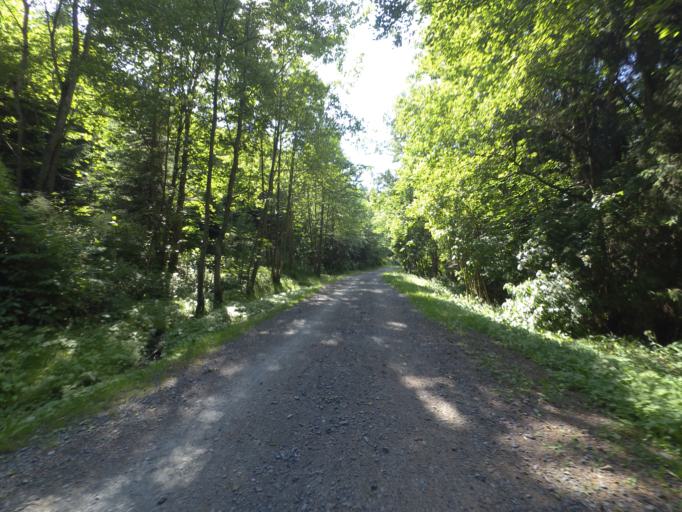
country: AT
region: Carinthia
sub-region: Politischer Bezirk Spittal an der Drau
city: Millstatt
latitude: 46.7741
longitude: 13.6019
